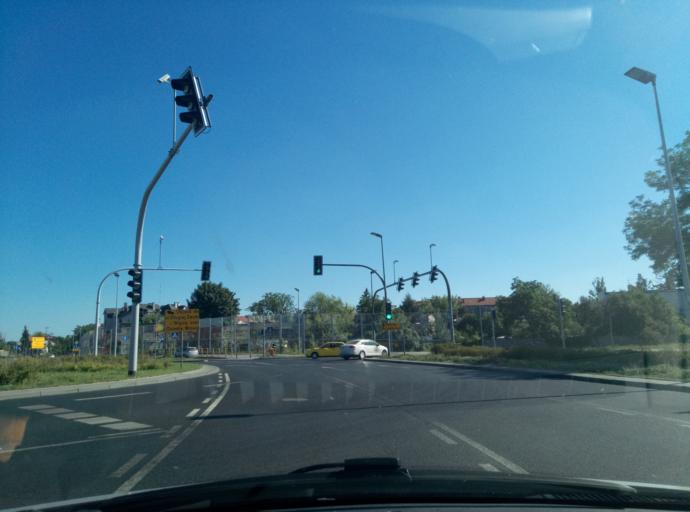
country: PL
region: Kujawsko-Pomorskie
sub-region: Torun
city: Torun
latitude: 53.0250
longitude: 18.5914
